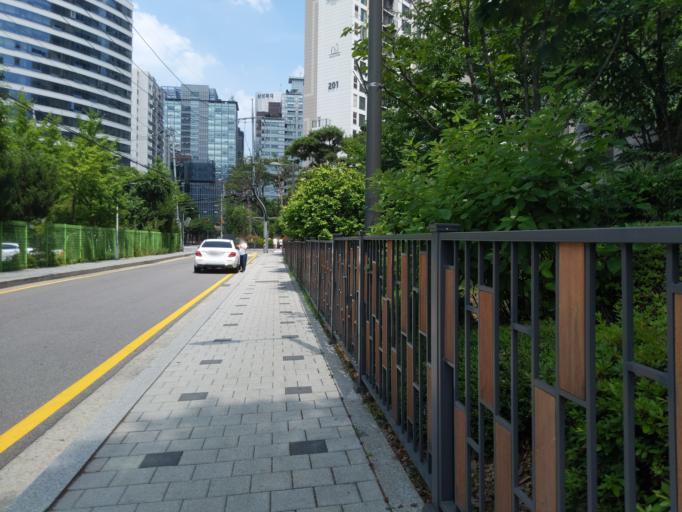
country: KR
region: Seoul
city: Seoul
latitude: 37.4934
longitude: 127.0251
